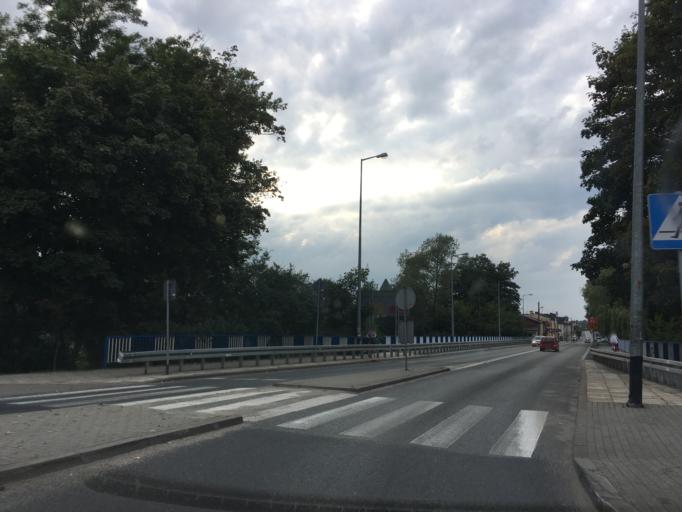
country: PL
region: Lodz Voivodeship
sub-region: Powiat radomszczanski
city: Przedborz
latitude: 51.0880
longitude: 19.8738
